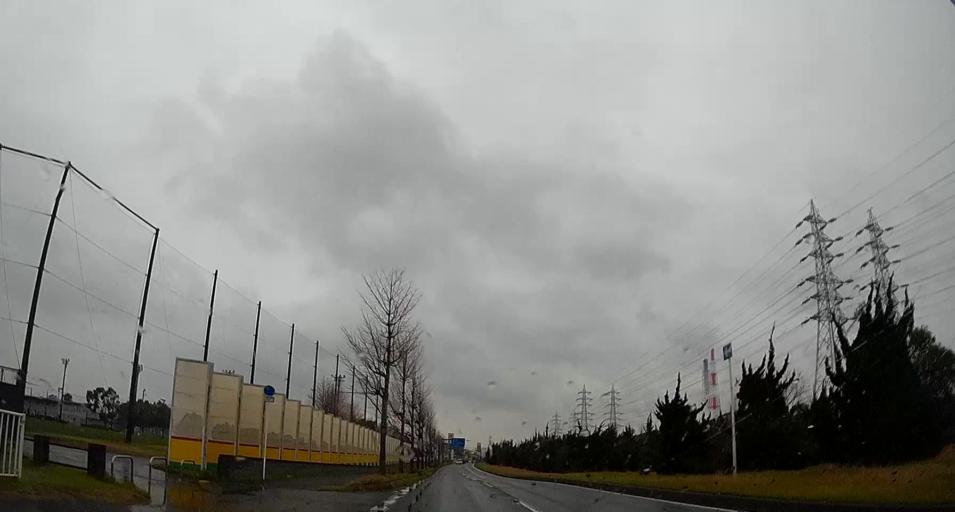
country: JP
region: Chiba
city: Ichihara
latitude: 35.4909
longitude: 140.0435
